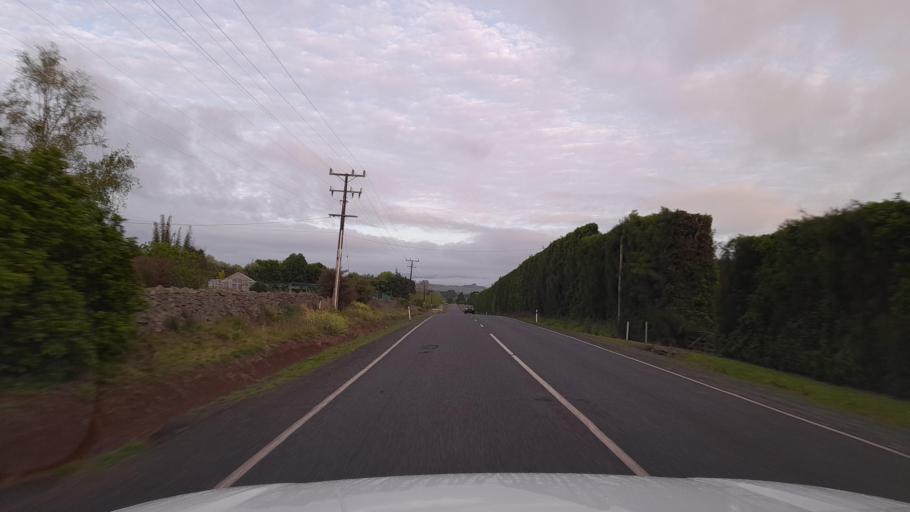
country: NZ
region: Northland
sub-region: Whangarei
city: Maungatapere
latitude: -35.7430
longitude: 174.1500
